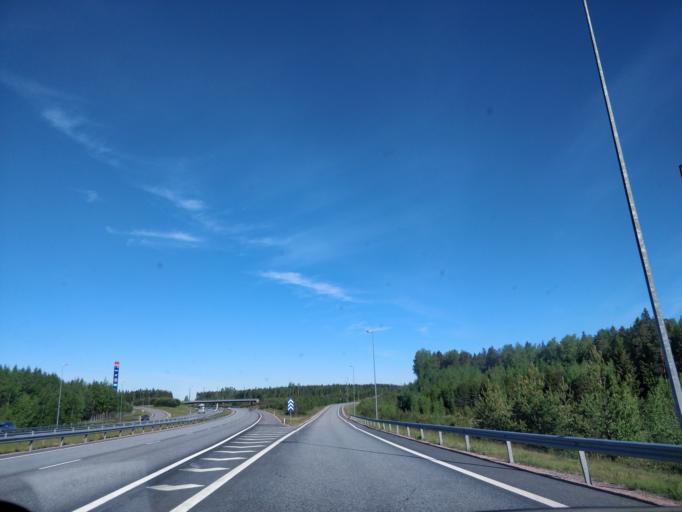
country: FI
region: Varsinais-Suomi
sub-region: Salo
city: Suomusjaervi
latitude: 60.3800
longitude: 23.6265
